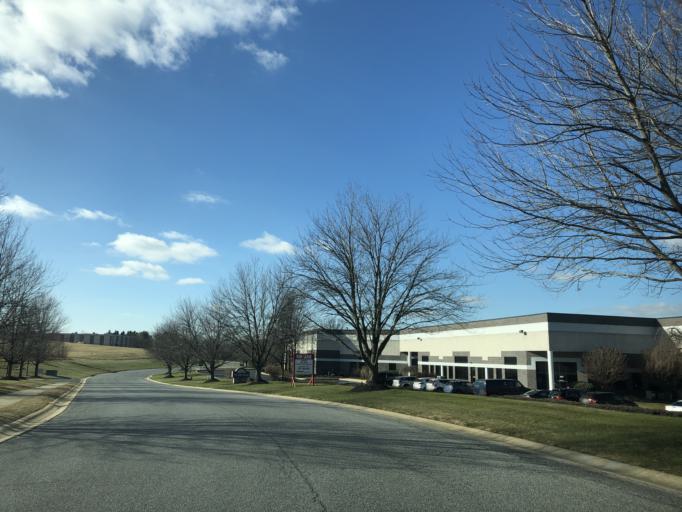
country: US
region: Pennsylvania
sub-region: Chester County
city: Coatesville
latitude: 39.9942
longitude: -75.8676
